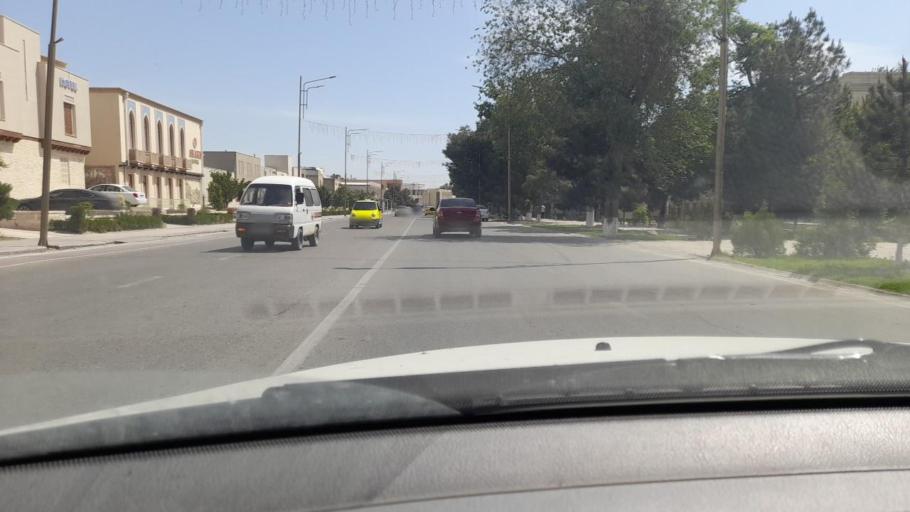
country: UZ
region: Bukhara
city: Bukhara
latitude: 39.7729
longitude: 64.4276
